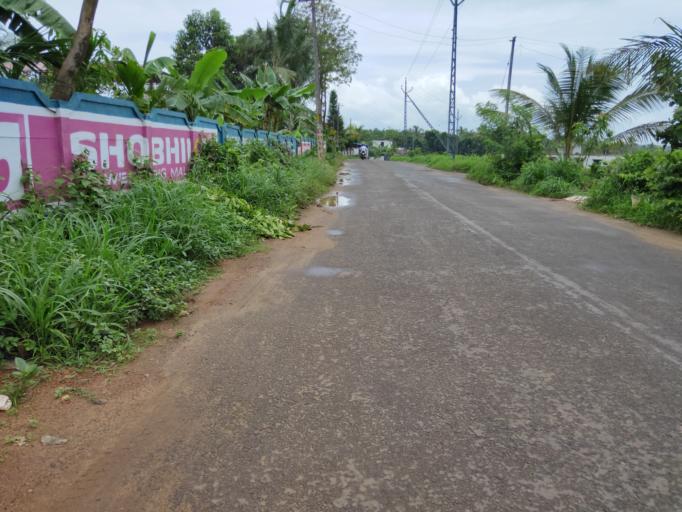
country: IN
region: Kerala
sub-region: Malappuram
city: Manjeri
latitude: 11.2312
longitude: 76.2814
